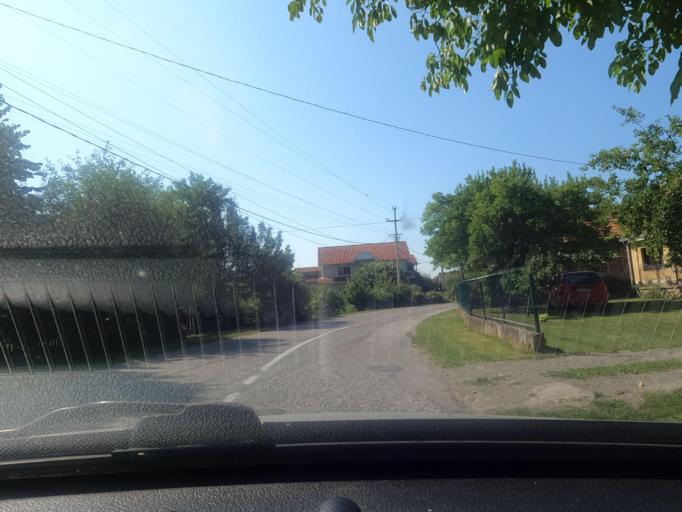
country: RS
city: Lipnicki Sor
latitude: 44.5779
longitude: 19.2710
